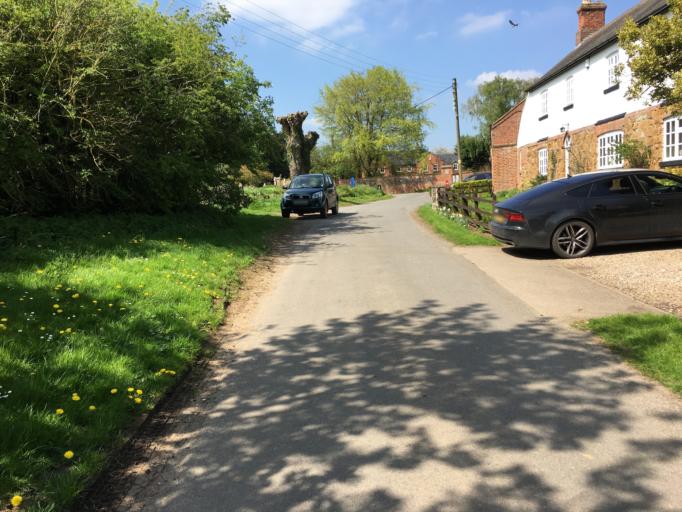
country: GB
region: England
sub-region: Leicestershire
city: Houghton on the Hill
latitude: 52.6026
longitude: -0.9744
